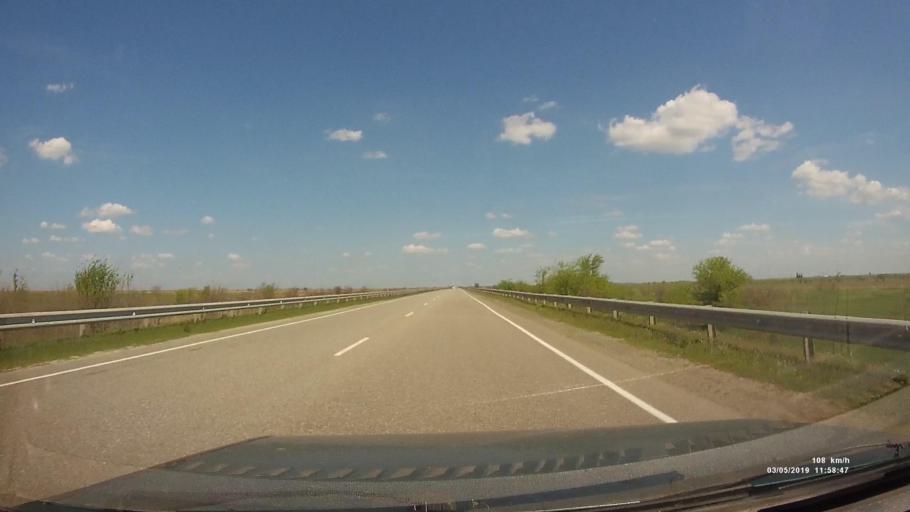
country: RU
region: Rostov
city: Bagayevskaya
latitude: 47.2256
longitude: 40.3235
